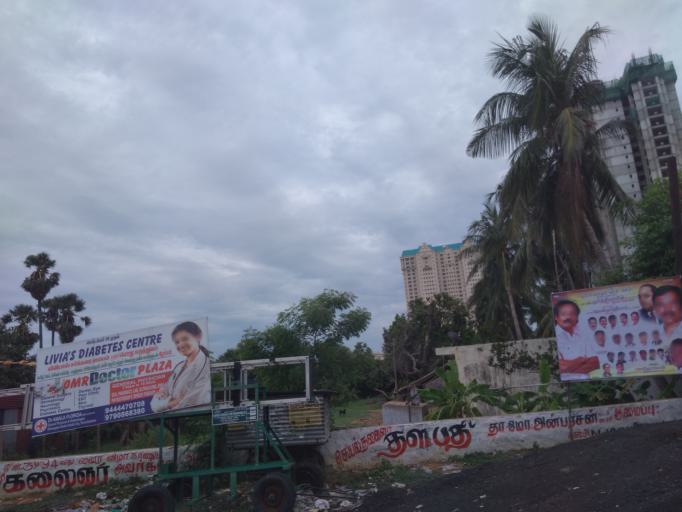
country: IN
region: Tamil Nadu
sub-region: Kancheepuram
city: Injambakkam
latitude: 12.8391
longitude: 80.2280
